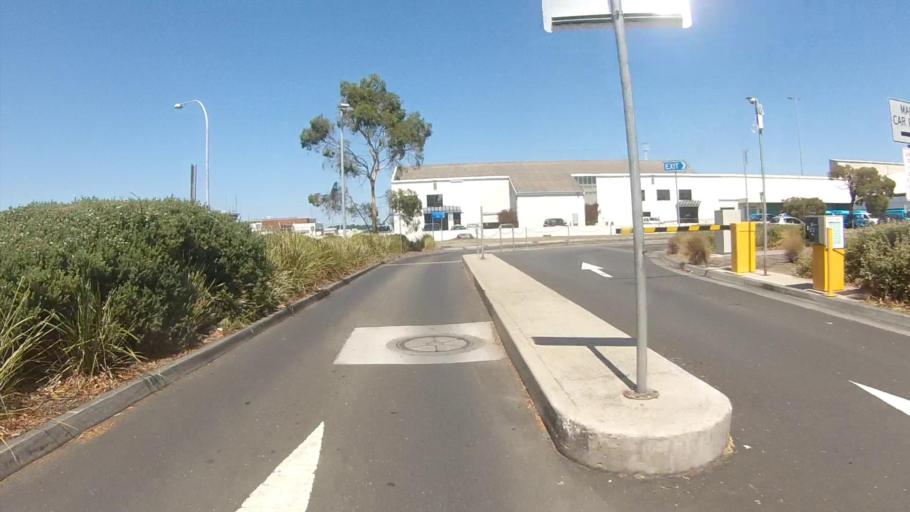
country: AU
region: Tasmania
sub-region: Clarence
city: Seven Mile Beach
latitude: -42.8383
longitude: 147.5064
